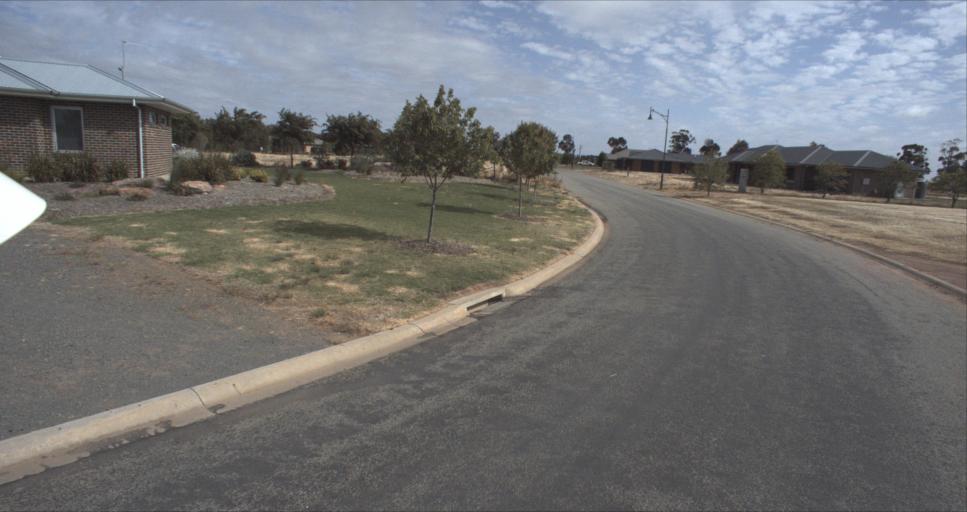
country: AU
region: New South Wales
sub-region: Leeton
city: Leeton
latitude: -34.5601
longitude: 146.4283
